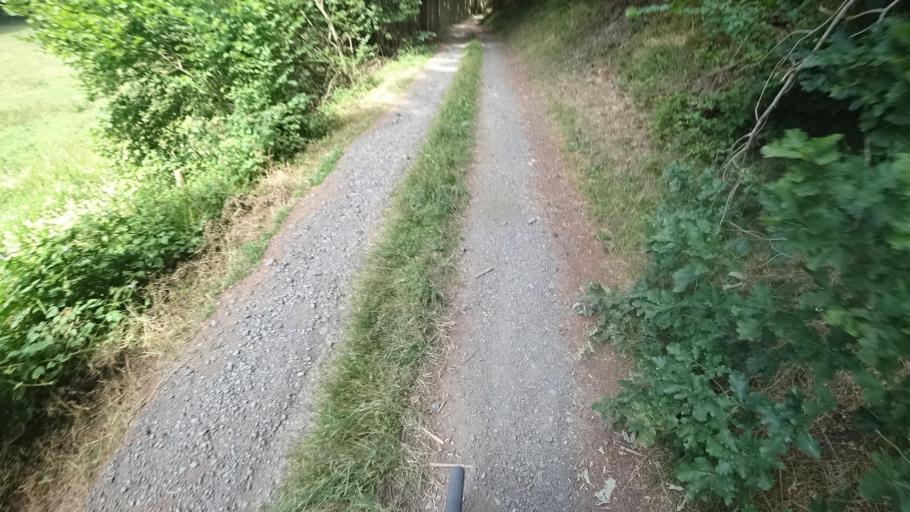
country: DE
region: Rheinland-Pfalz
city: Heckenbach
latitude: 50.4822
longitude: 7.0830
